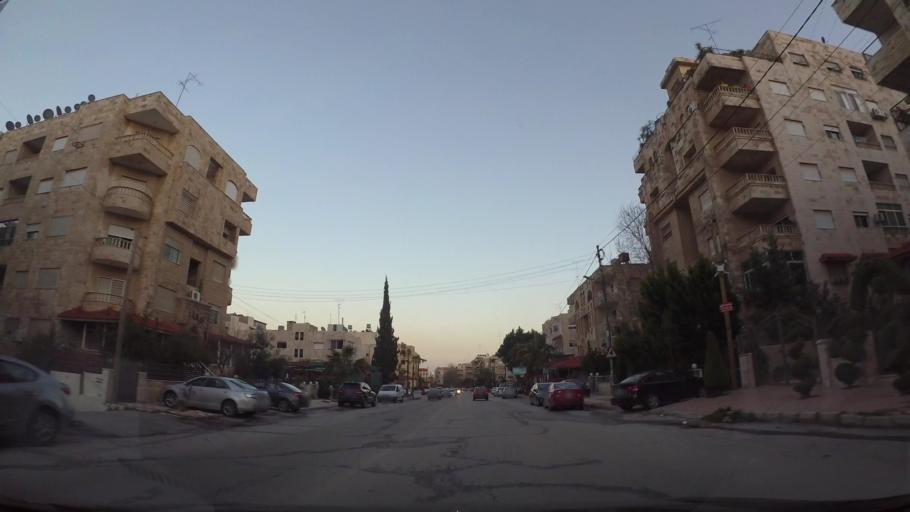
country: JO
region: Amman
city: Al Jubayhah
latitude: 31.9890
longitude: 35.8809
